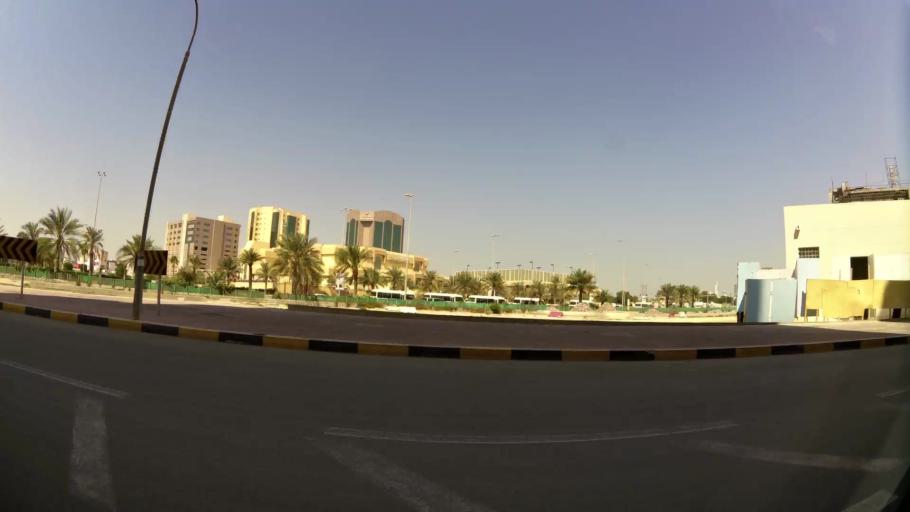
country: BH
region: Manama
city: Manama
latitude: 26.2149
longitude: 50.5978
